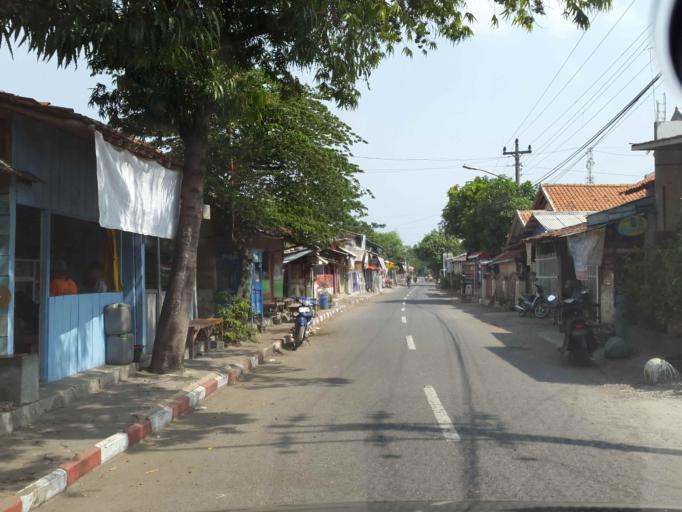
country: ID
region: Central Java
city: Dukuhturi
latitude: -6.8757
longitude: 109.0565
